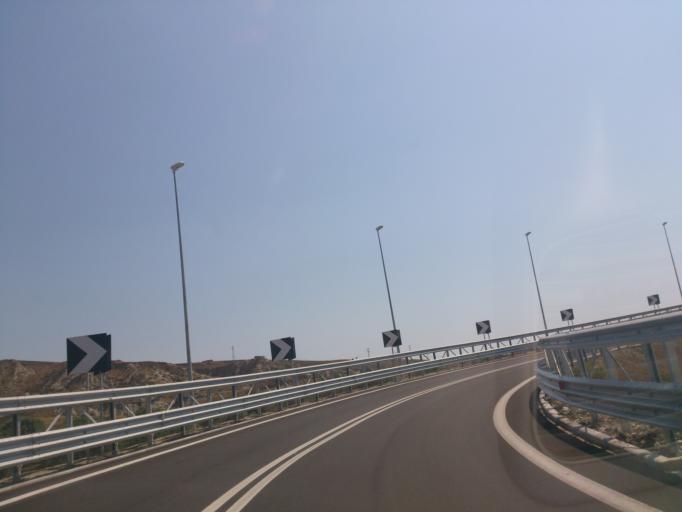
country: IT
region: Calabria
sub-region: Provincia di Reggio Calabria
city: Marina di Gioiosa Ionica
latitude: 38.3112
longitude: 16.3527
